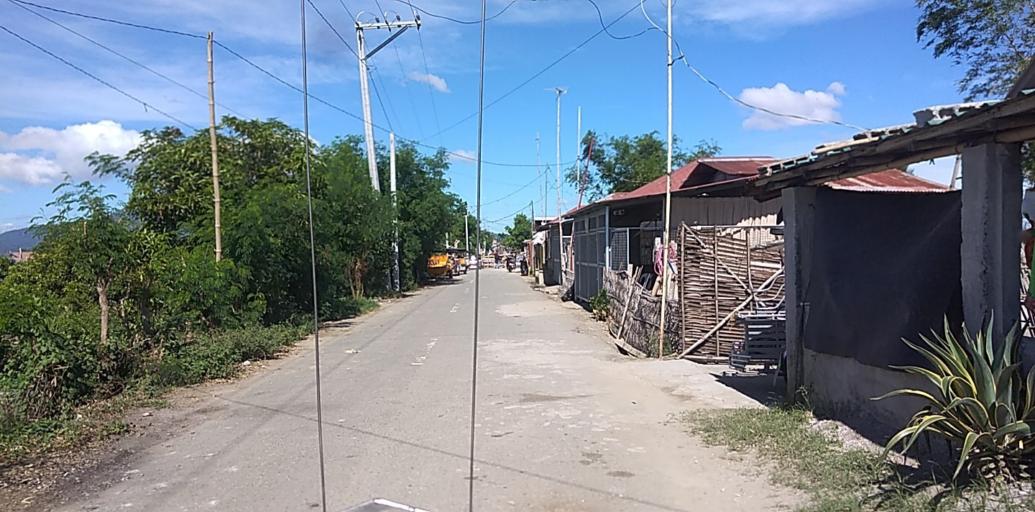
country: PH
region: Central Luzon
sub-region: Province of Pampanga
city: Candating
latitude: 15.1318
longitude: 120.8076
